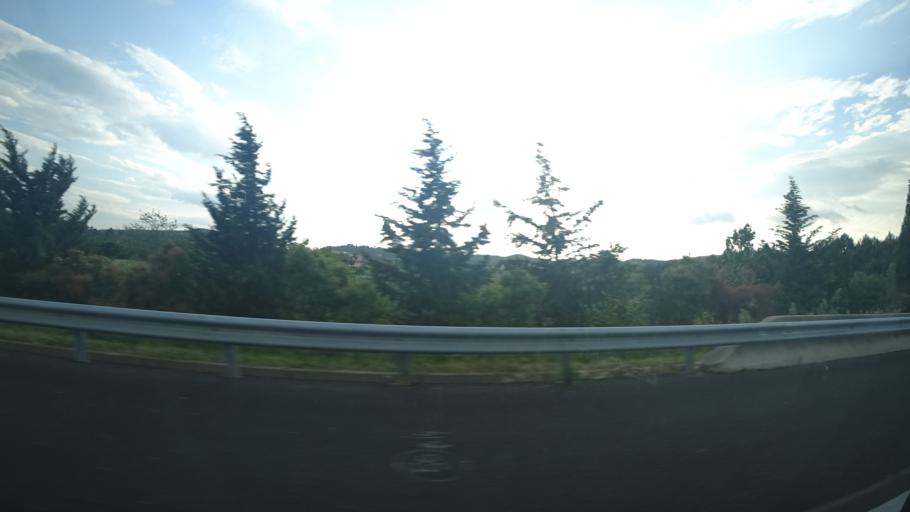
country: FR
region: Languedoc-Roussillon
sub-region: Departement de l'Herault
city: Nebian
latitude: 43.6341
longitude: 3.4475
